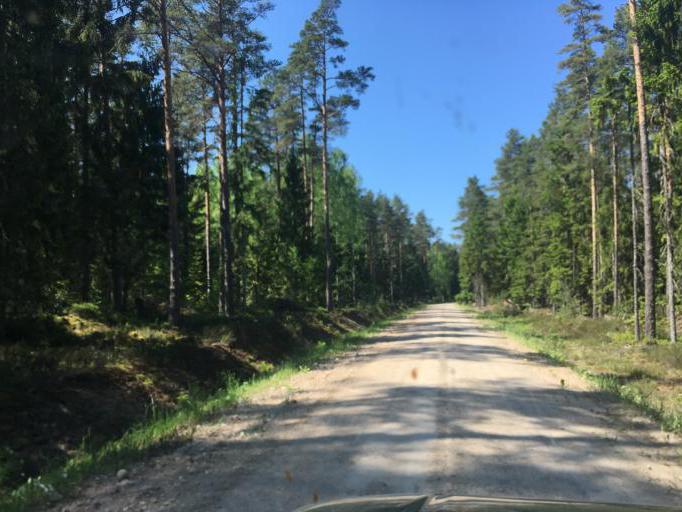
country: LV
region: Talsu Rajons
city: Valdemarpils
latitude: 57.4334
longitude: 22.6889
